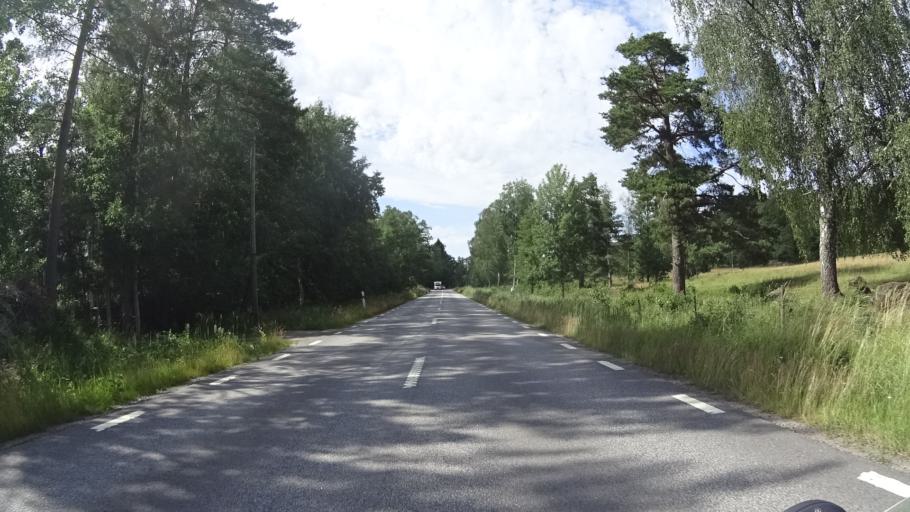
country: SE
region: OEstergoetland
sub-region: Atvidabergs Kommun
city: Atvidaberg
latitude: 58.0972
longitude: 16.1231
